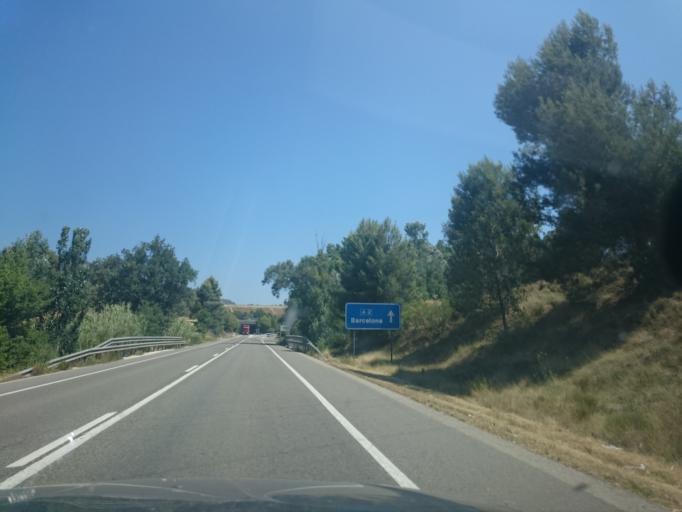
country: ES
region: Catalonia
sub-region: Provincia de Barcelona
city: Odena
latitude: 41.5842
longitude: 1.6720
